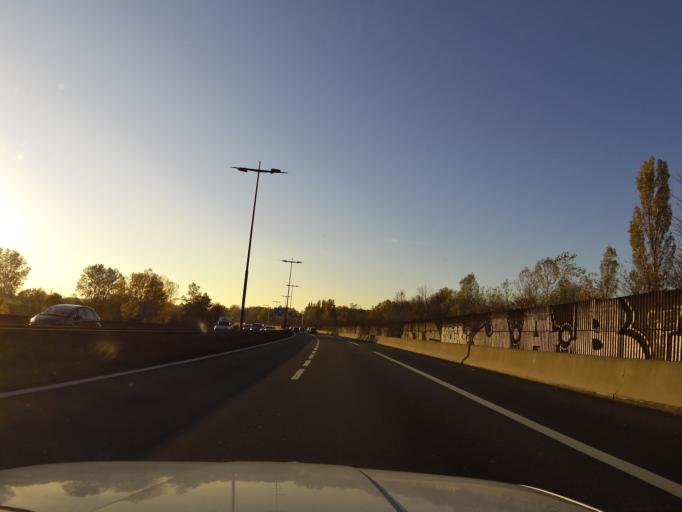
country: FR
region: Rhone-Alpes
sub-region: Departement du Rhone
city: Vaulx-en-Velin
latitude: 45.7967
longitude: 4.9433
